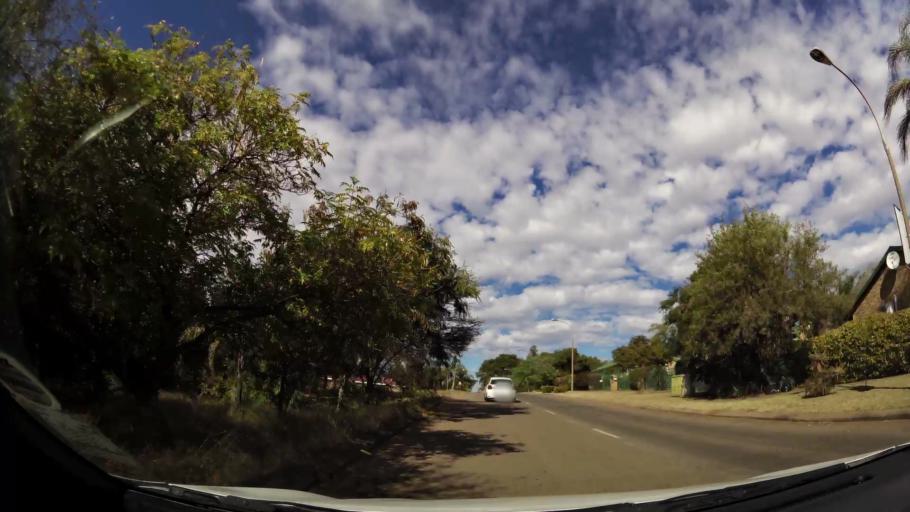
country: ZA
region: Limpopo
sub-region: Waterberg District Municipality
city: Warmbaths
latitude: -24.8705
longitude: 28.2903
